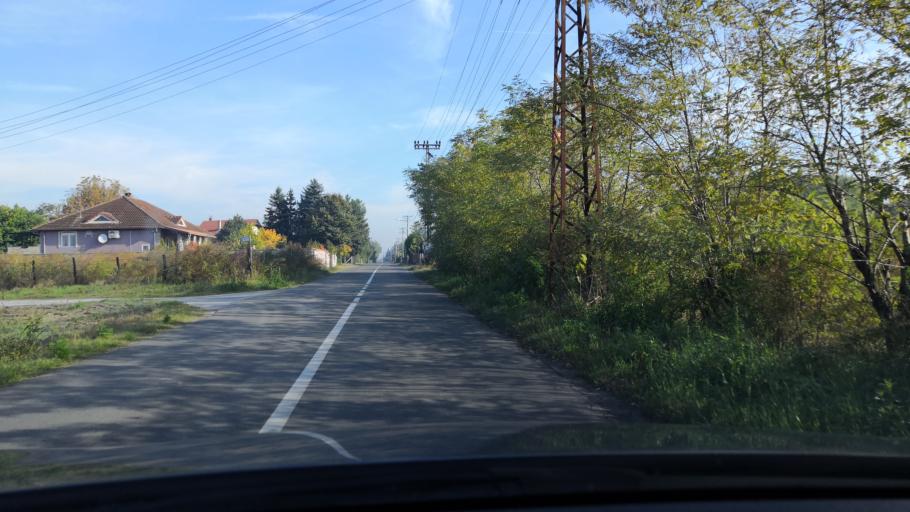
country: HU
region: Csongrad
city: Asotthalom
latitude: 46.1141
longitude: 19.8404
